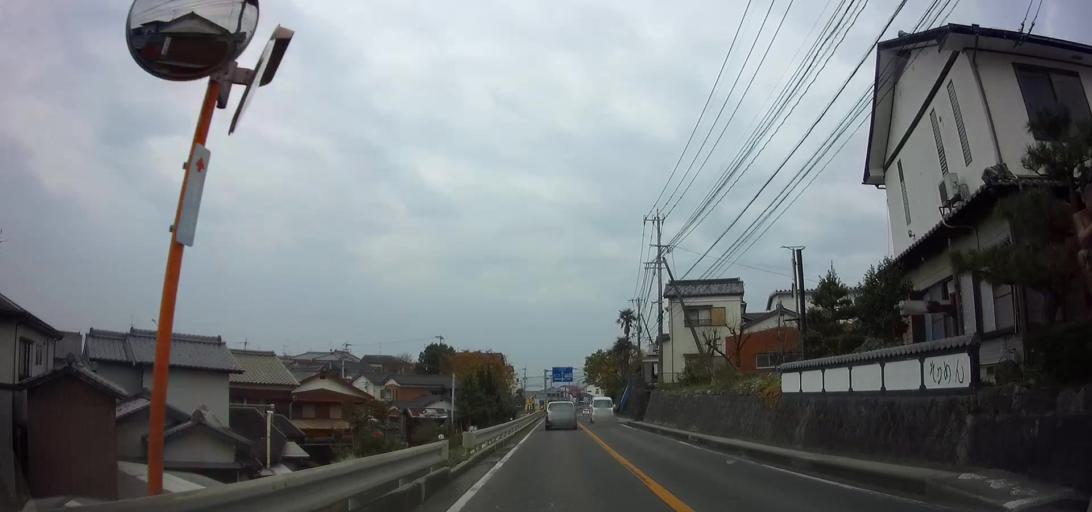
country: JP
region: Nagasaki
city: Shimabara
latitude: 32.6548
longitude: 130.2902
